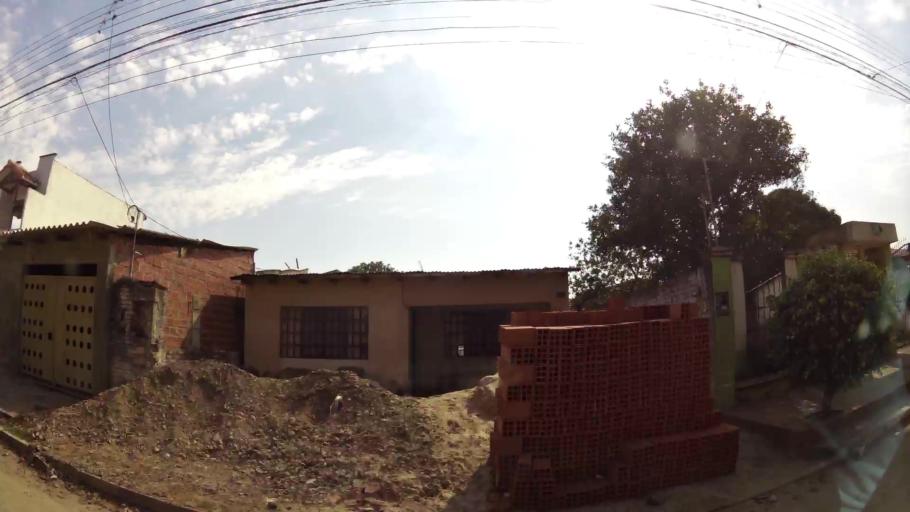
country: BO
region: Santa Cruz
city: Santa Cruz de la Sierra
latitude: -17.7268
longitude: -63.1538
